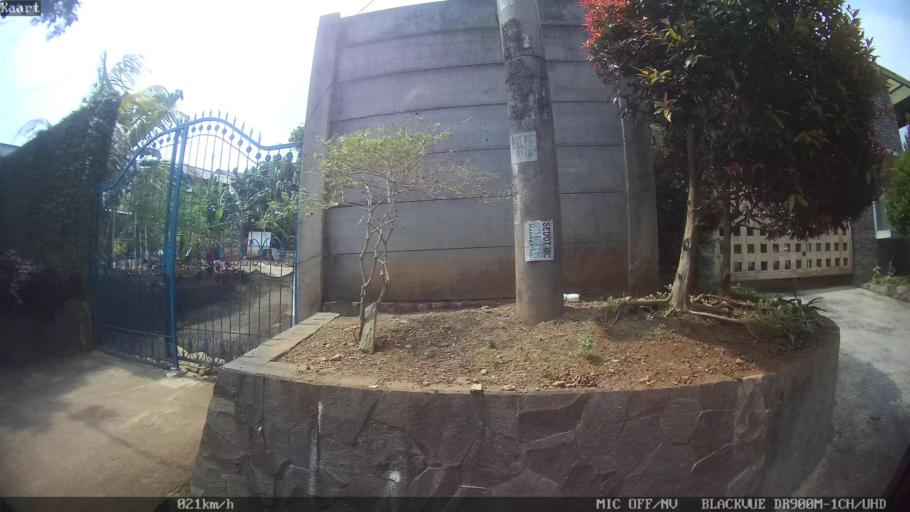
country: ID
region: Lampung
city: Bandarlampung
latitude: -5.4333
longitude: 105.2676
